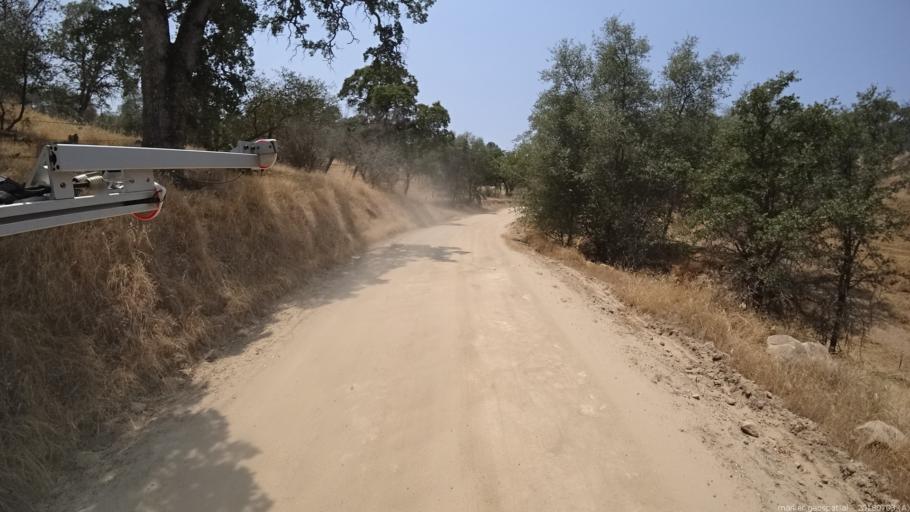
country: US
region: California
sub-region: Madera County
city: Yosemite Lakes
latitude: 37.0690
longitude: -119.6691
